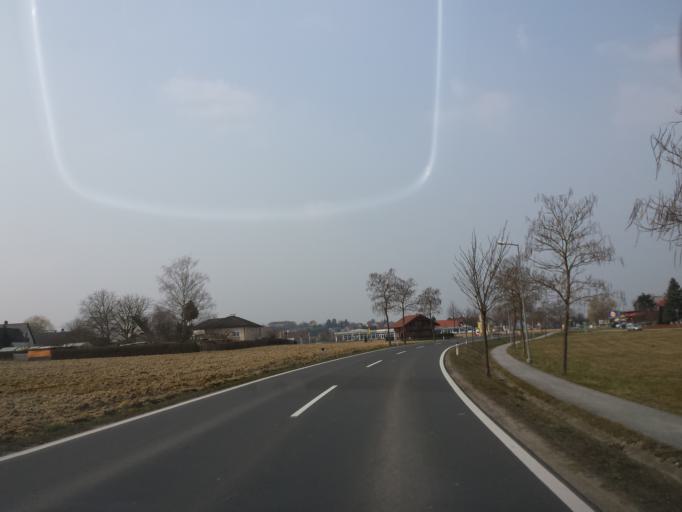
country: AT
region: Styria
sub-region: Politischer Bezirk Hartberg-Fuerstenfeld
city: Fuerstenfeld
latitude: 47.0293
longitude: 16.0895
